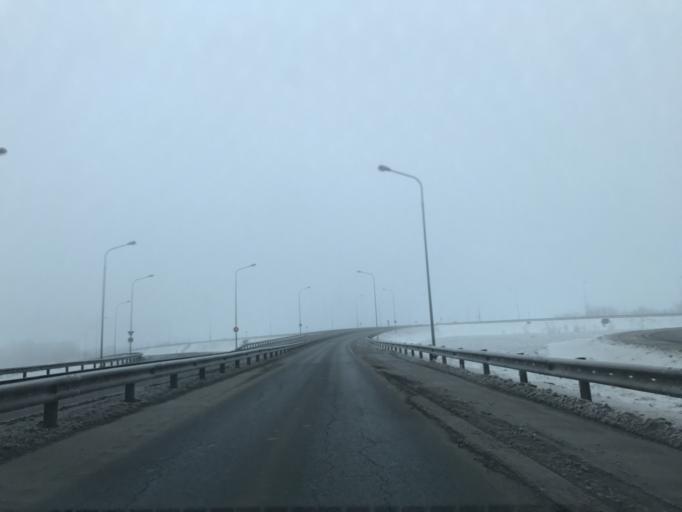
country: RU
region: Rostov
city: Grushevskaya
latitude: 47.3788
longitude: 39.9028
